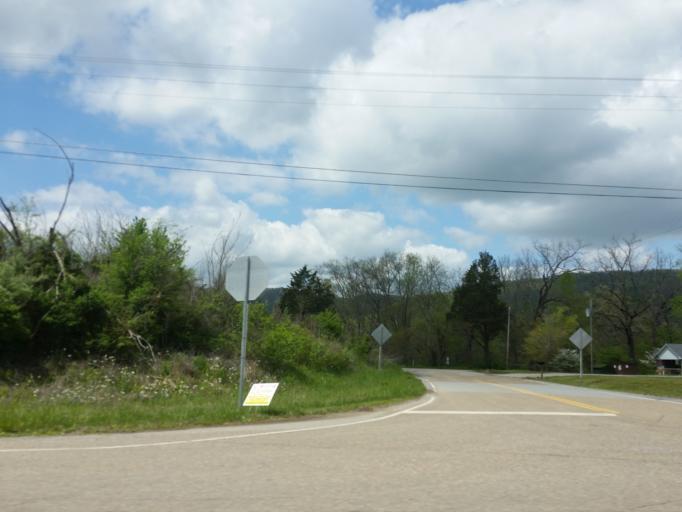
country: US
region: Kentucky
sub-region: Bell County
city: Middlesboro
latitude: 36.5285
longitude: -83.7345
